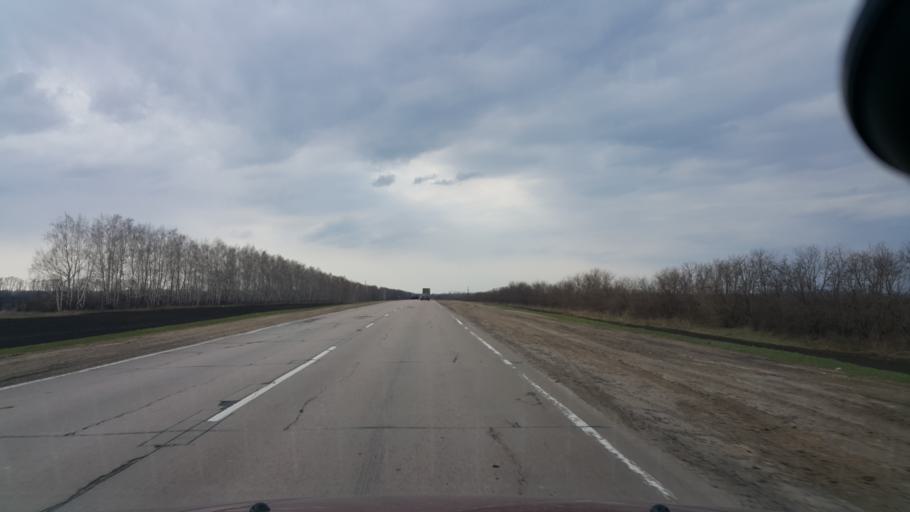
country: RU
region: Tambov
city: Znamenka
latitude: 52.4254
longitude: 41.3750
